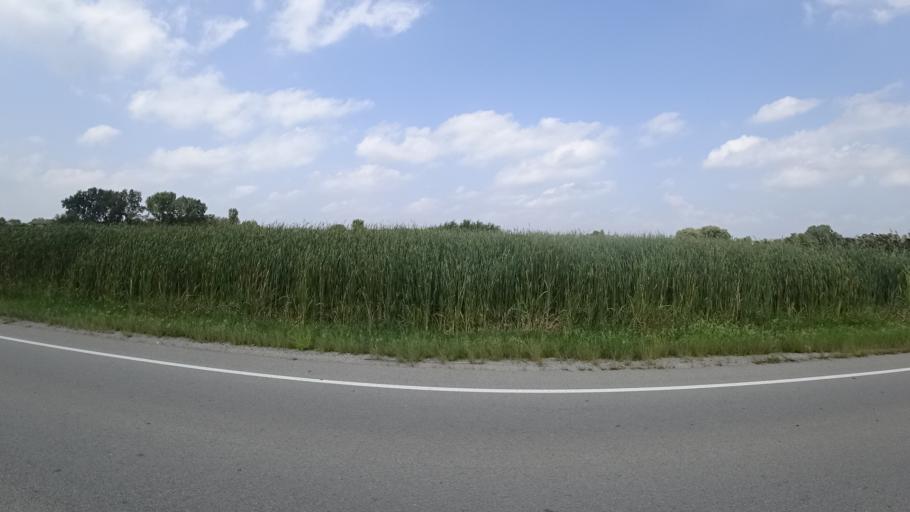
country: US
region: Illinois
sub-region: Will County
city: Goodings Grove
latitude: 41.6296
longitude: -87.8982
